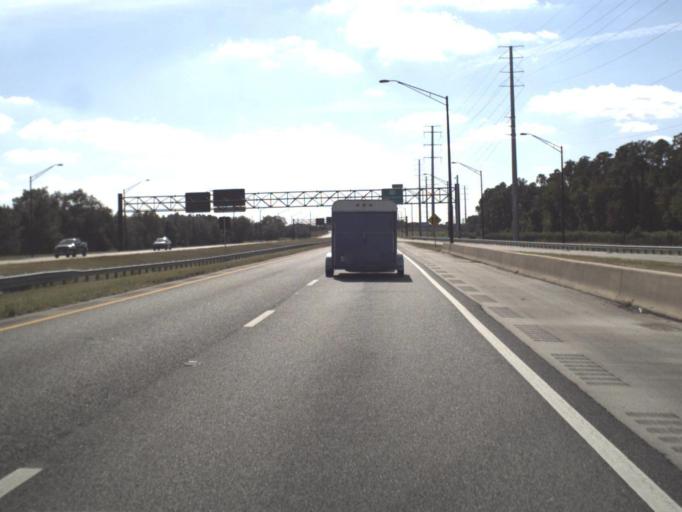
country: US
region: Florida
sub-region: Polk County
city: Citrus Ridge
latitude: 28.3578
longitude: -81.6126
